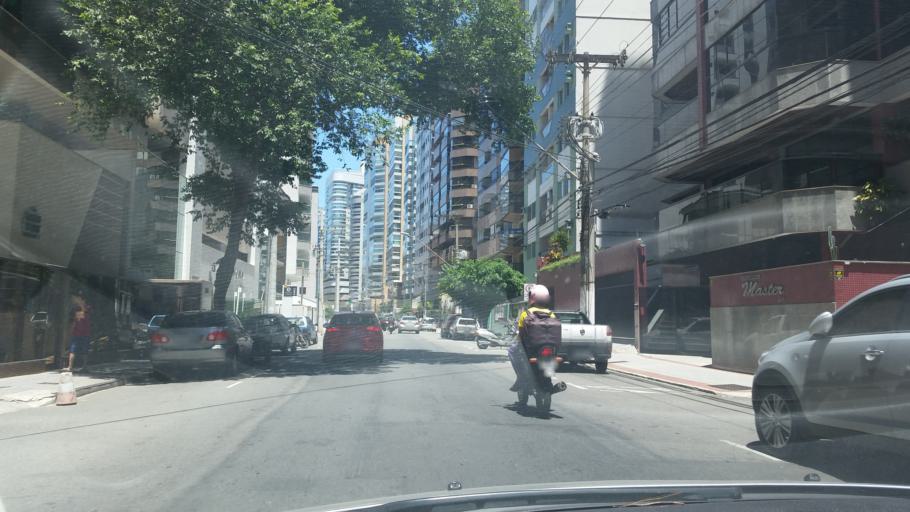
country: BR
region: Espirito Santo
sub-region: Vila Velha
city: Vila Velha
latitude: -20.3326
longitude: -40.2796
